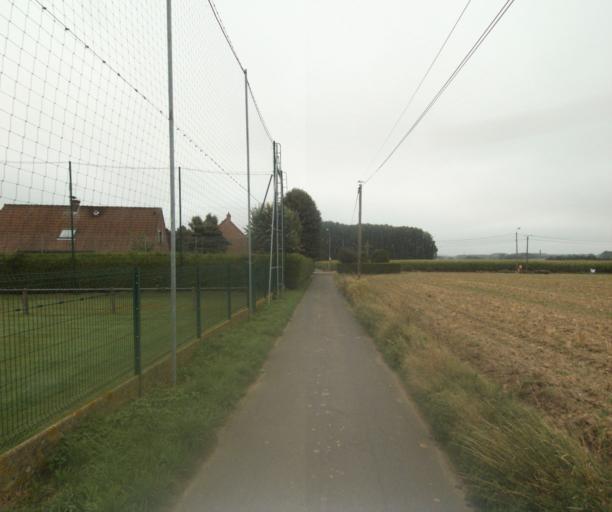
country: FR
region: Nord-Pas-de-Calais
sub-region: Departement du Nord
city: Sailly-lez-Lannoy
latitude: 50.6448
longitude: 3.2153
